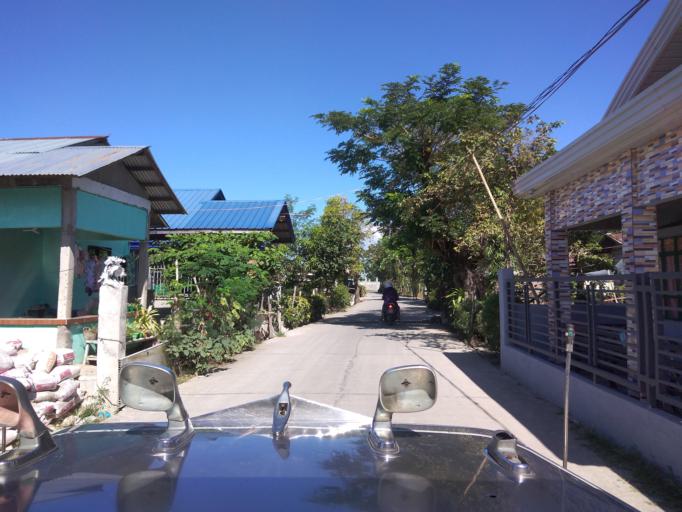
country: PH
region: Central Luzon
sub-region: Province of Pampanga
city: Batasan Bata
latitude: 15.1650
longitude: 120.9184
